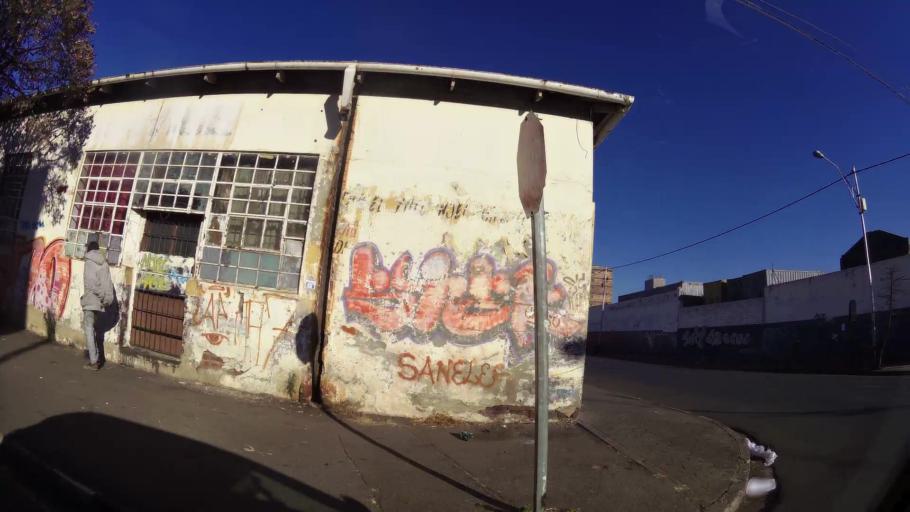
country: ZA
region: Gauteng
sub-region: City of Johannesburg Metropolitan Municipality
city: Johannesburg
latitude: -26.2062
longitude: 28.0602
